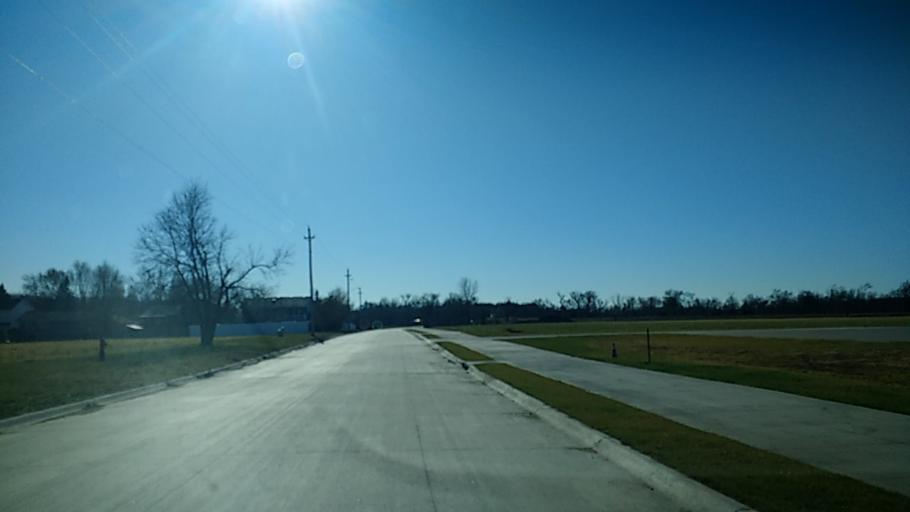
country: US
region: South Dakota
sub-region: Union County
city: North Sioux City
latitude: 42.5443
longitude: -96.5267
